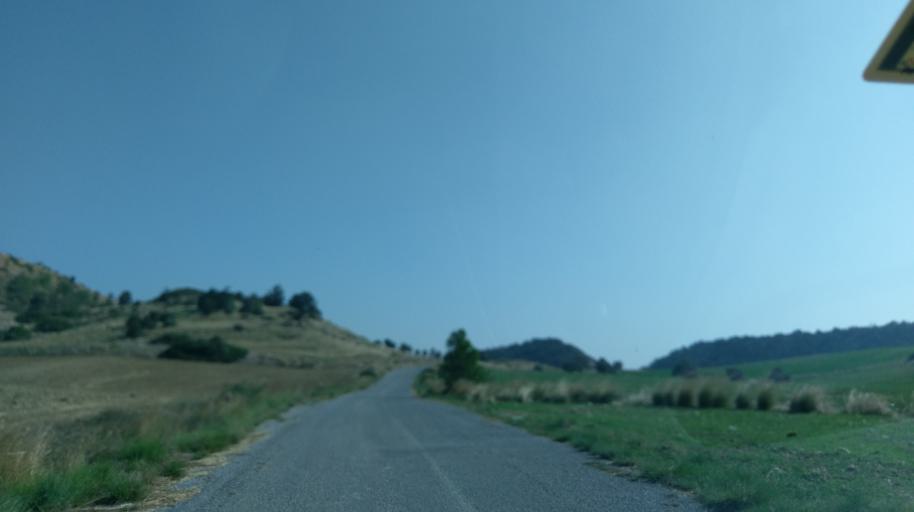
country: CY
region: Ammochostos
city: Lefkonoiko
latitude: 35.3215
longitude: 33.6706
